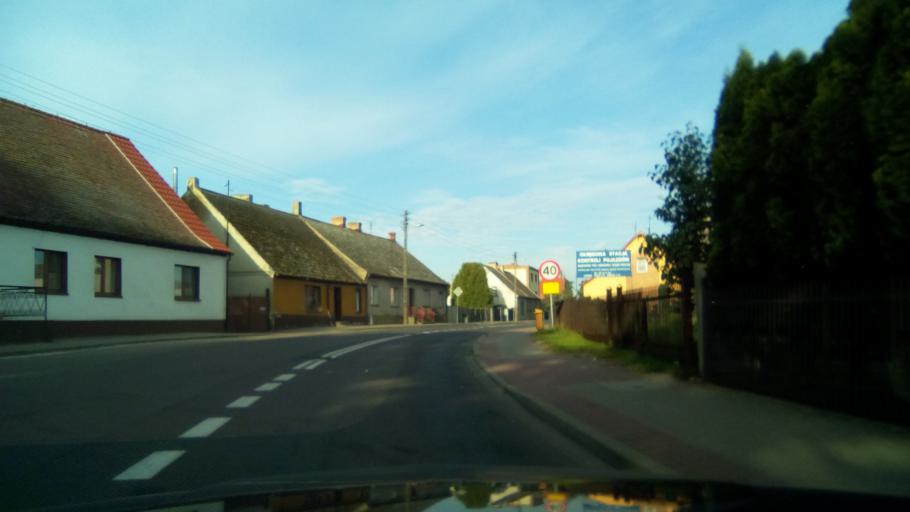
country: PL
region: Greater Poland Voivodeship
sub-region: Powiat wagrowiecki
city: Miescisko
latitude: 52.7437
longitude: 17.3268
